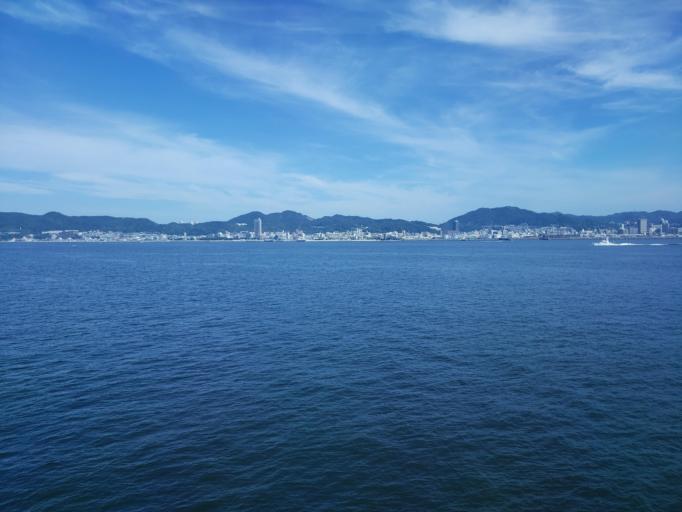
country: JP
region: Hyogo
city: Kobe
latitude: 34.6244
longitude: 135.1464
